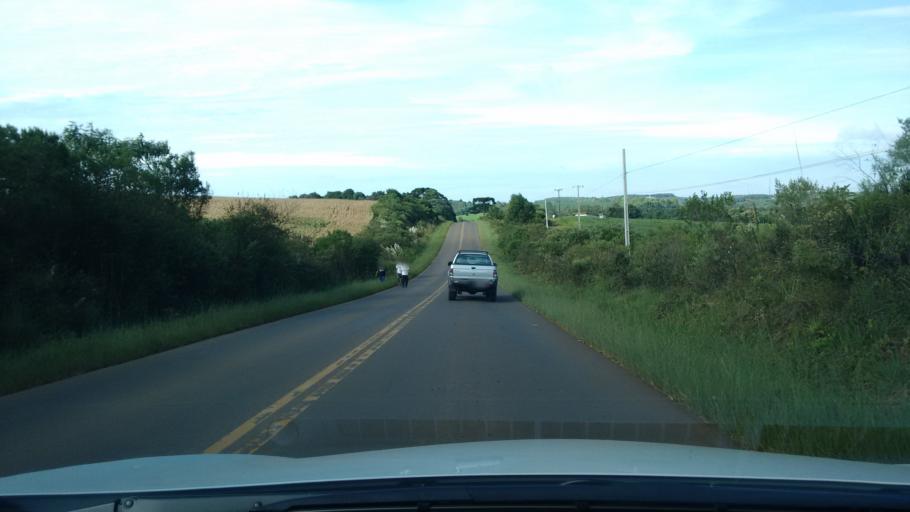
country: BR
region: Santa Catarina
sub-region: Videira
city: Videira
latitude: -27.0789
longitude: -50.8997
